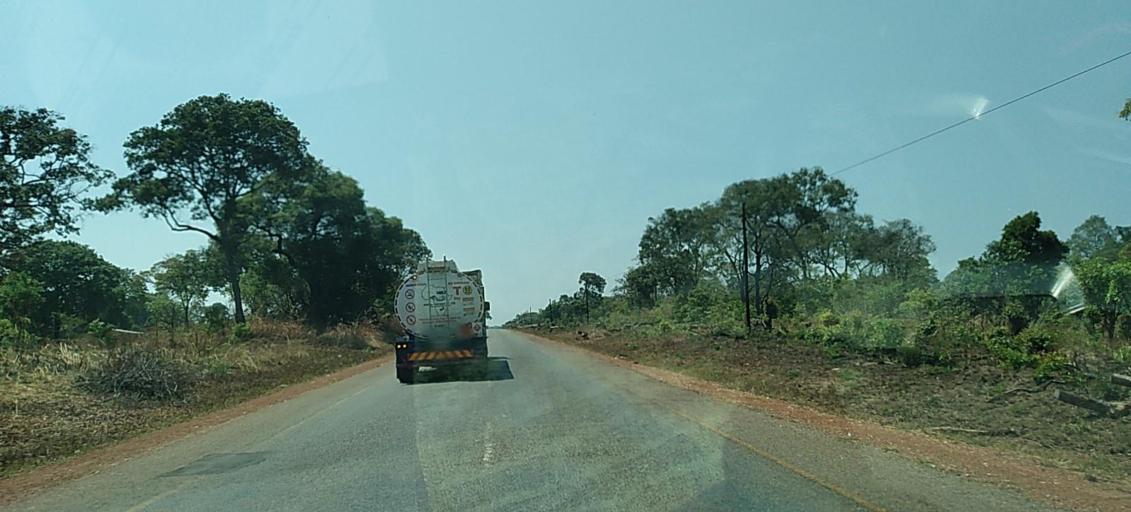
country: ZM
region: North-Western
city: Solwezi
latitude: -12.3488
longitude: 25.9172
